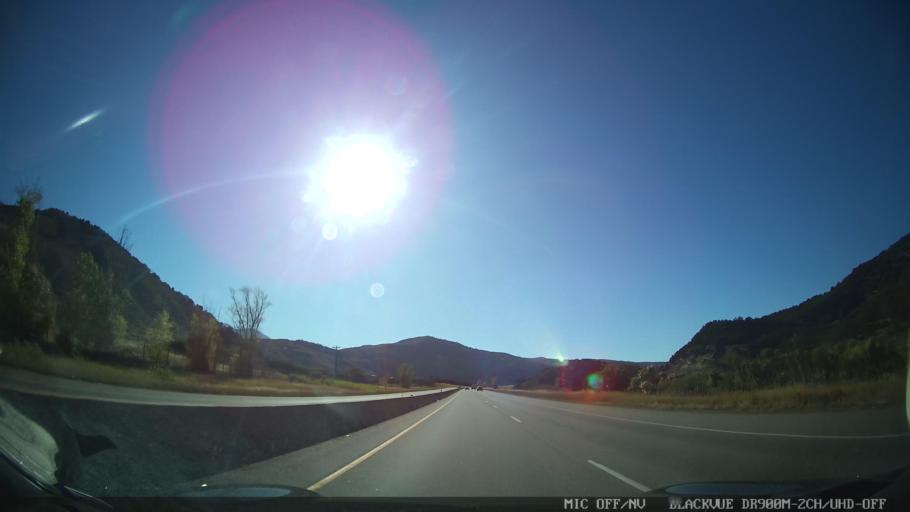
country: US
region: Colorado
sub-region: Eagle County
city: Basalt
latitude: 39.3665
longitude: -107.0527
